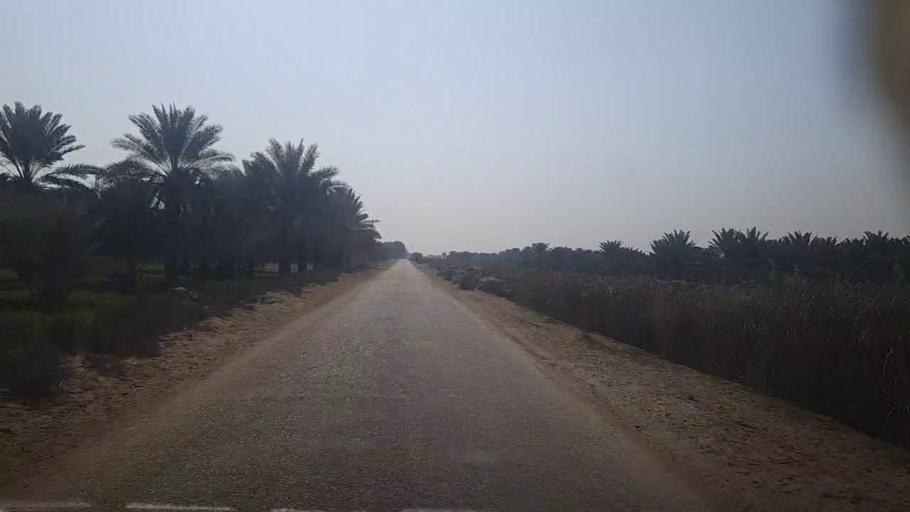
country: PK
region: Sindh
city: Khairpur
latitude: 27.4545
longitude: 68.8136
